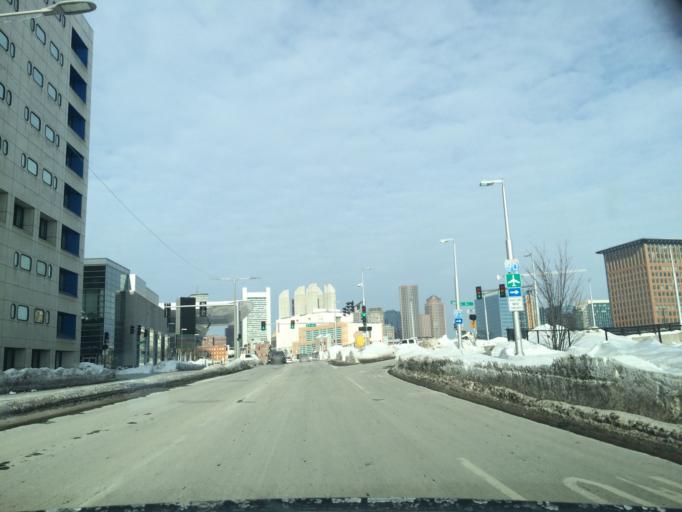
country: US
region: Massachusetts
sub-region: Suffolk County
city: South Boston
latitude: 42.3459
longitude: -71.0414
